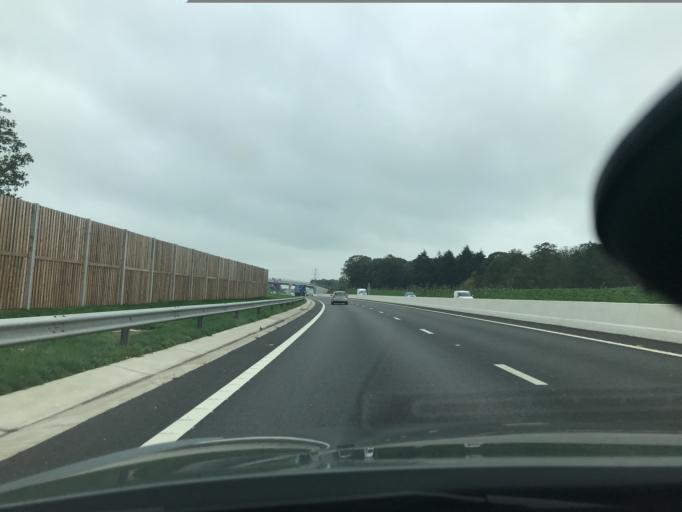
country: GB
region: England
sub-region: Cheshire East
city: Mere
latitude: 53.3288
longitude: -2.4224
